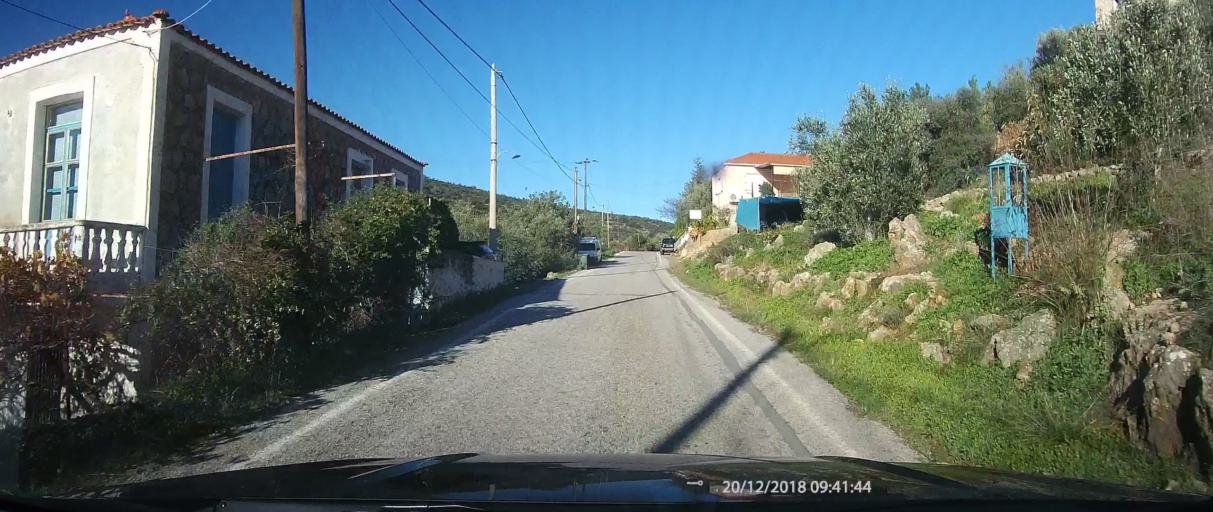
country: GR
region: Peloponnese
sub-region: Nomos Lakonias
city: Yerakion
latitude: 36.9535
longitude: 22.7615
